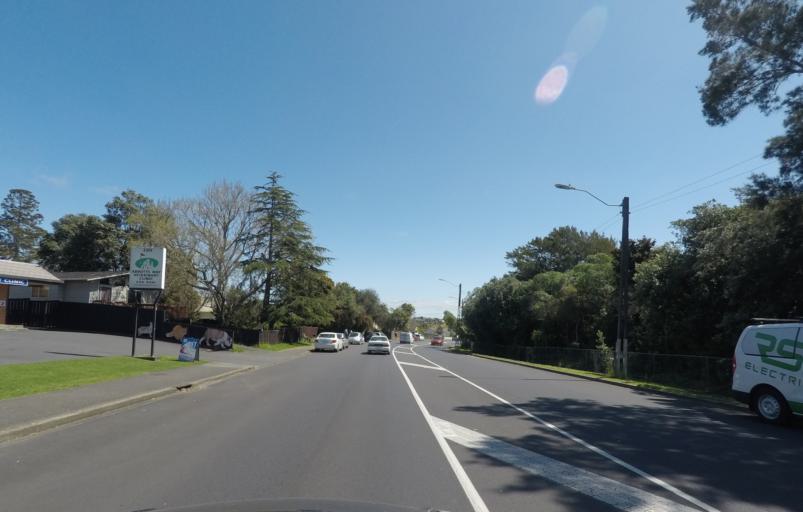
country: NZ
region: Auckland
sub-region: Auckland
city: Tamaki
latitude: -36.8875
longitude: 174.8282
